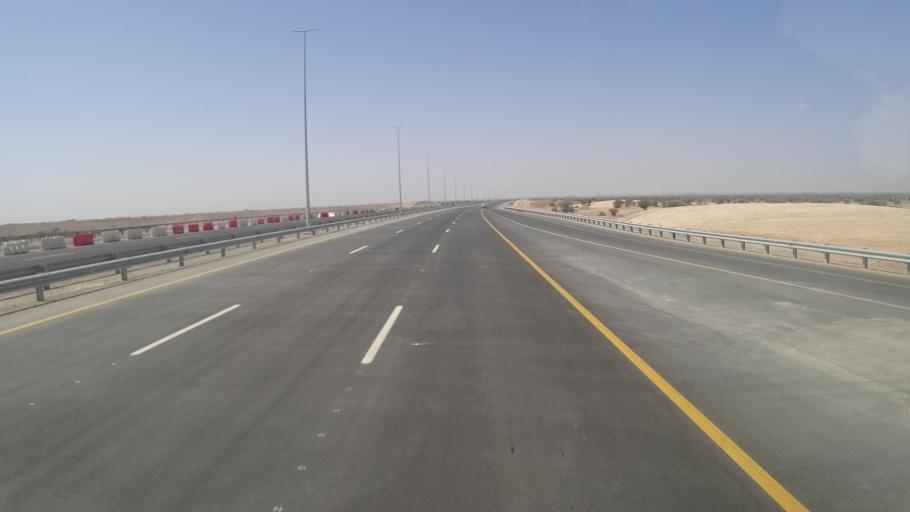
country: OM
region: Ash Sharqiyah
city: Sur
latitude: 22.2779
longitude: 59.2635
